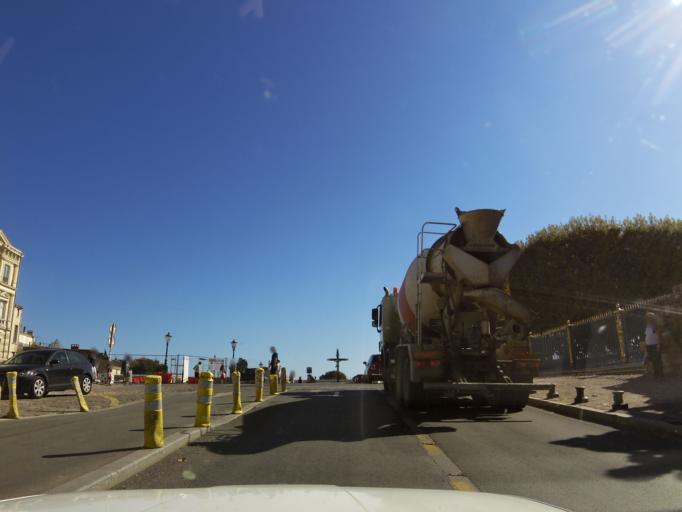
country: FR
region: Languedoc-Roussillon
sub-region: Departement de l'Herault
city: Montpellier
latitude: 43.6114
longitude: 3.8720
